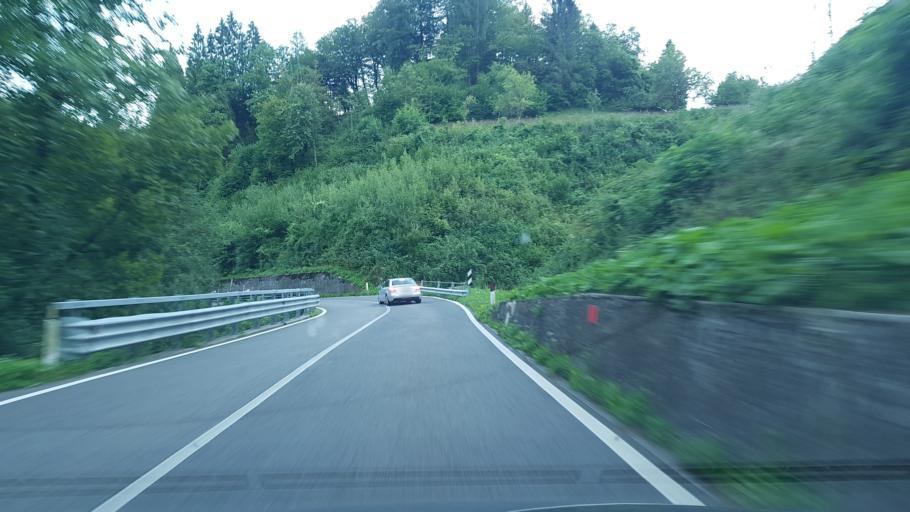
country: IT
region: Friuli Venezia Giulia
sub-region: Provincia di Udine
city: Comeglians
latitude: 46.5225
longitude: 12.8693
